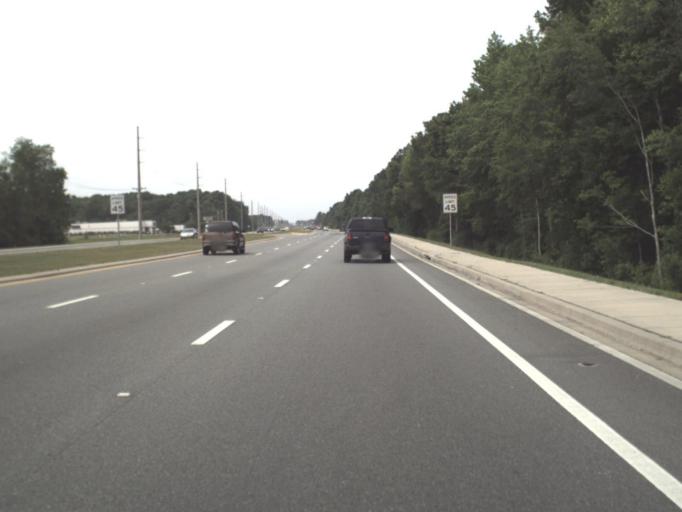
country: US
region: Florida
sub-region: Clay County
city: Lakeside
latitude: 30.1211
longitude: -81.8021
